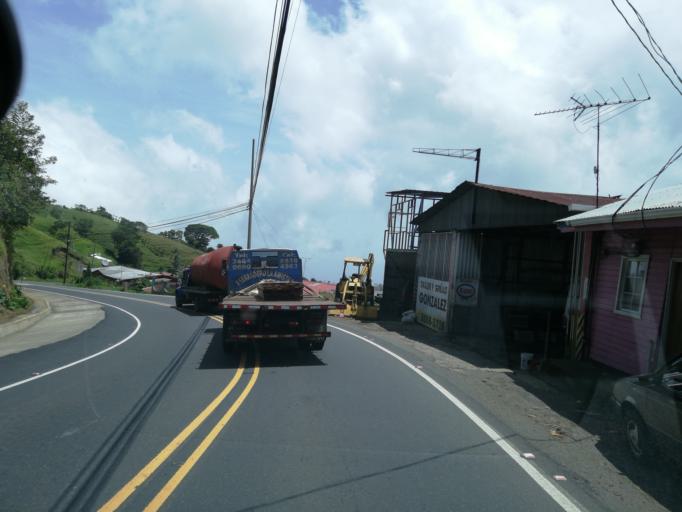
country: CR
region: Alajuela
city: Zarcero
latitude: 10.2189
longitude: -84.4029
